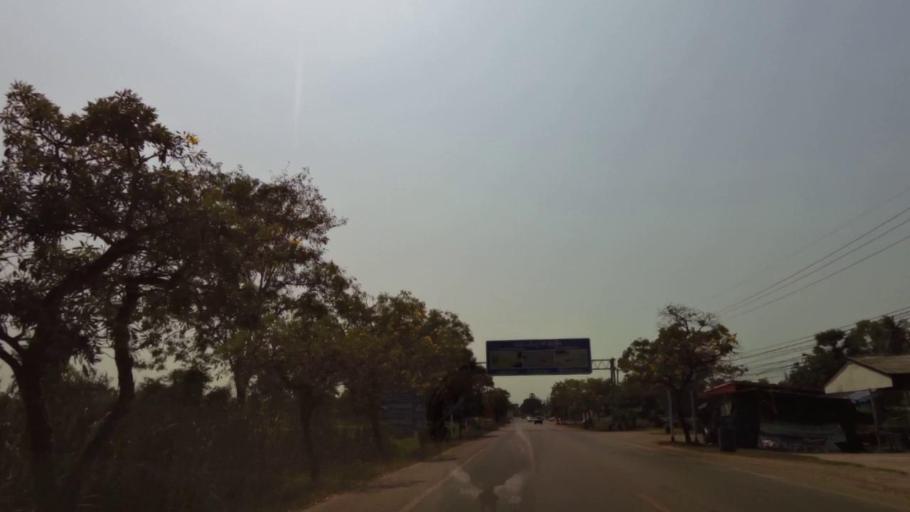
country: TH
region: Chanthaburi
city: Tha Mai
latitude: 12.5650
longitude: 101.9142
